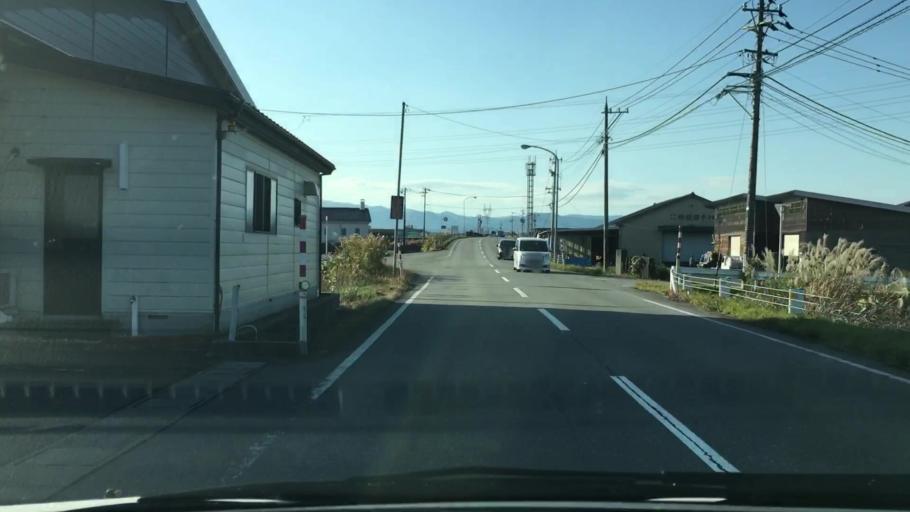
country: JP
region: Toyama
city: Kamiichi
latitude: 36.7082
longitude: 137.3174
